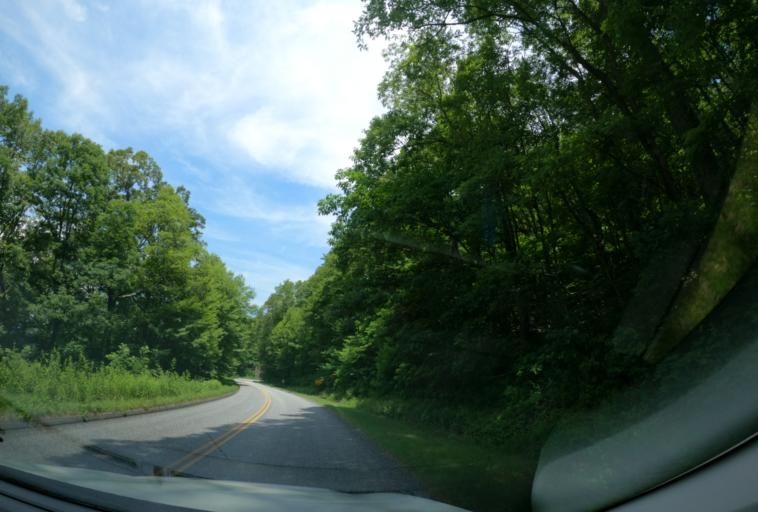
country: US
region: North Carolina
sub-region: Buncombe County
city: Bent Creek
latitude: 35.4485
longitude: -82.7163
